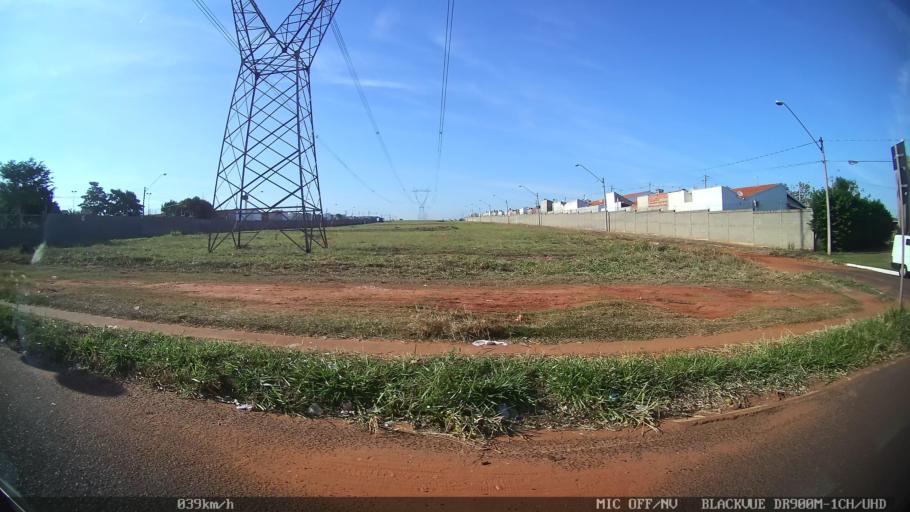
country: BR
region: Sao Paulo
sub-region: Sao Jose Do Rio Preto
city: Sao Jose do Rio Preto
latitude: -20.7700
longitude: -49.3288
